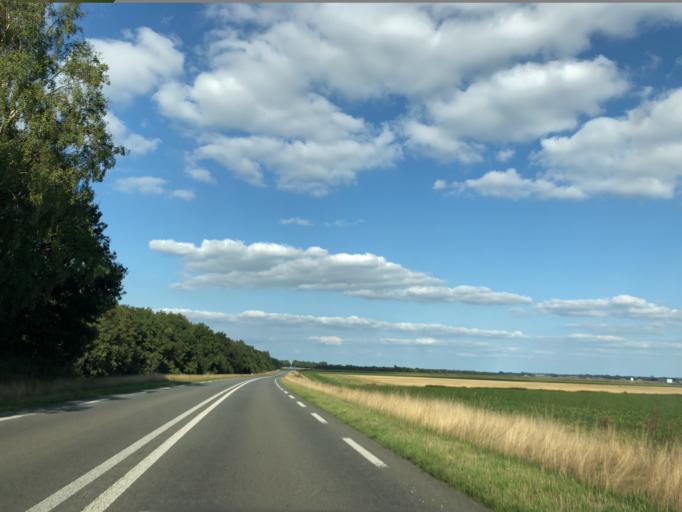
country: NL
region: Groningen
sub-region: Gemeente Stadskanaal
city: Stadskanaal
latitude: 52.9532
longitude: 6.8746
